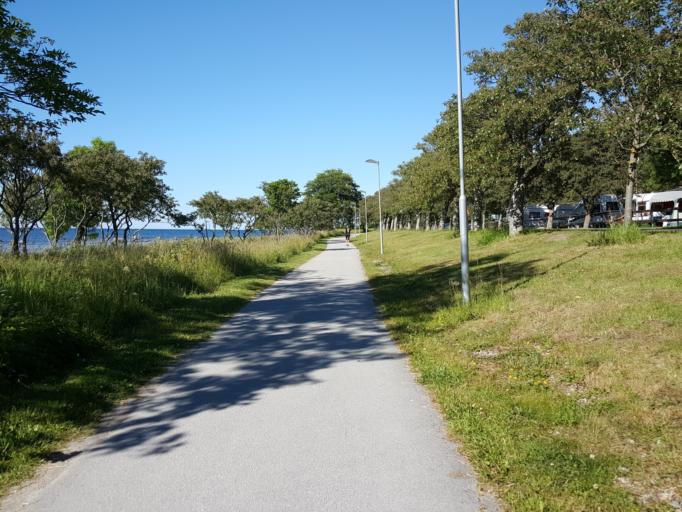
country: SE
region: Gotland
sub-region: Gotland
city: Visby
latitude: 57.6568
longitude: 18.3087
